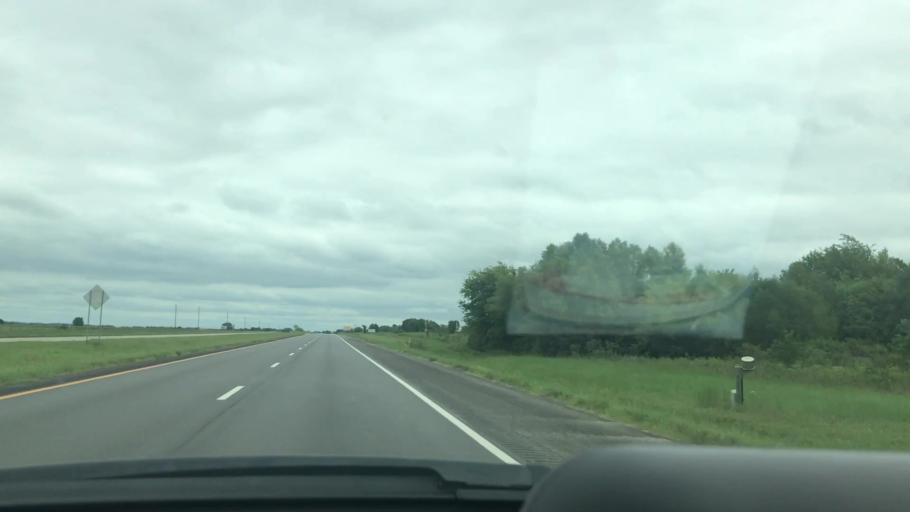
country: US
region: Oklahoma
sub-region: Mayes County
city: Pryor
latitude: 36.4497
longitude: -95.2666
